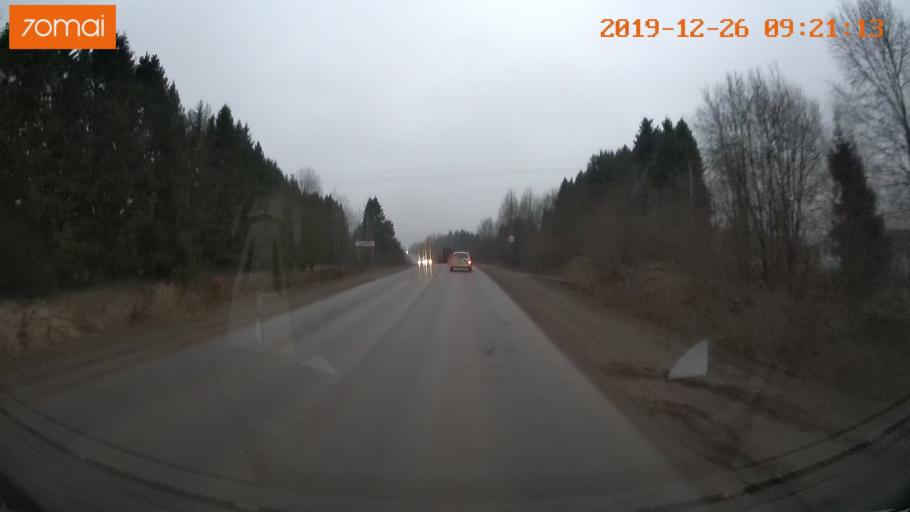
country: RU
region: Vologda
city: Gryazovets
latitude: 58.9687
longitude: 40.2256
